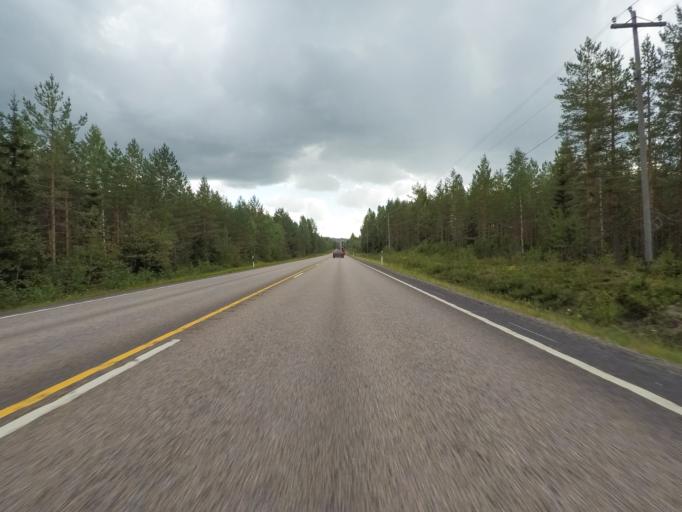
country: FI
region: Central Finland
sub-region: Joutsa
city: Leivonmaeki
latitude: 61.9460
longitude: 26.1100
